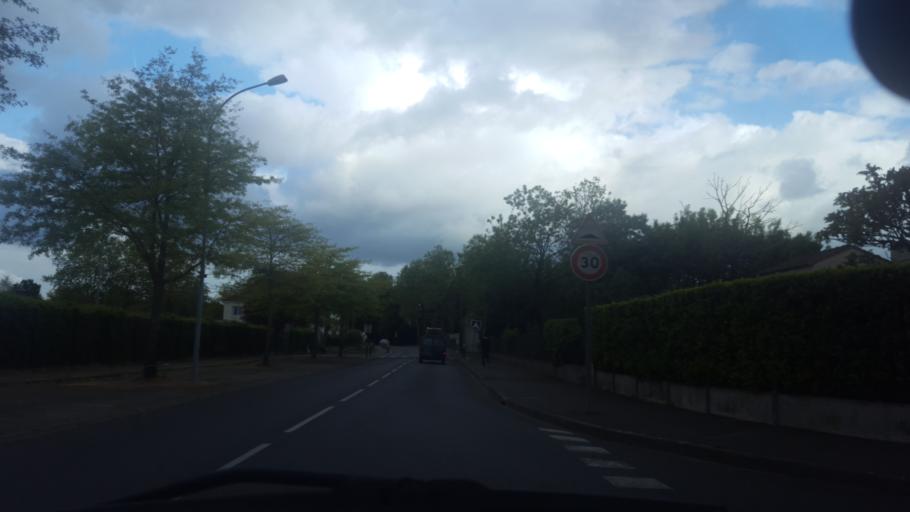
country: FR
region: Pays de la Loire
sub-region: Departement de la Loire-Atlantique
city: Saint-Philbert-de-Grand-Lieu
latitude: 47.0418
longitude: -1.6450
